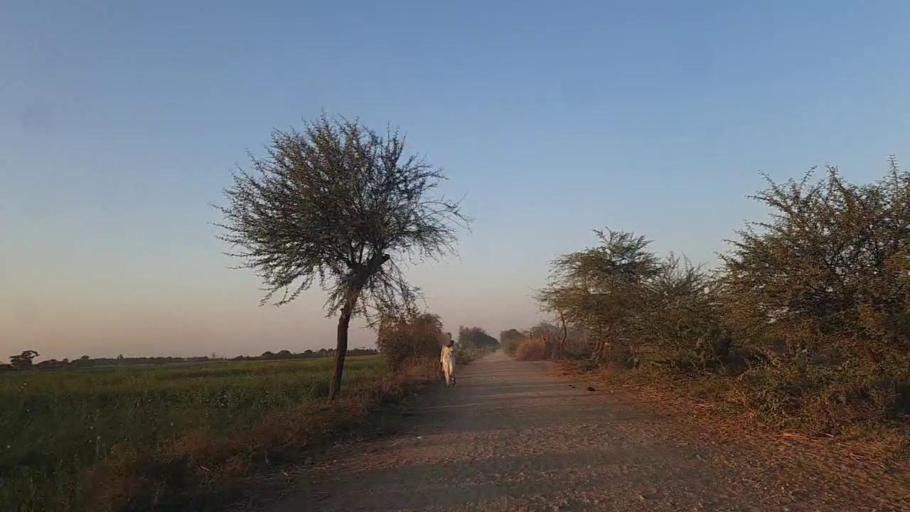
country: PK
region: Sindh
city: Naukot
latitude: 25.0511
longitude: 69.4070
